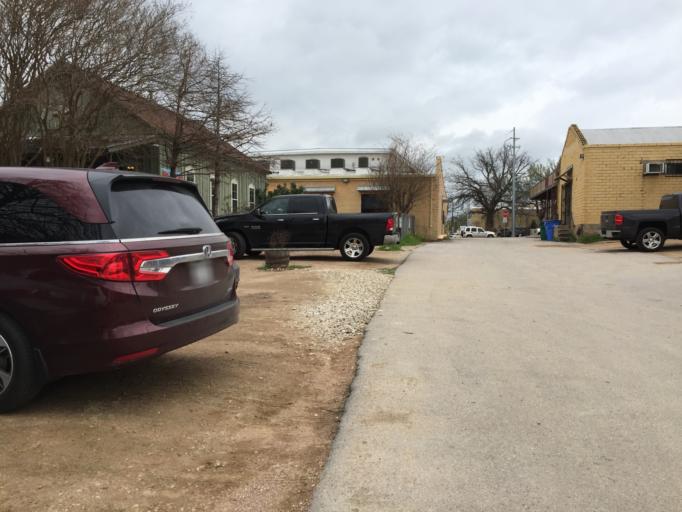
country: US
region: Texas
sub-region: Bastrop County
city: Bastrop
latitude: 30.1097
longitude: -97.3206
